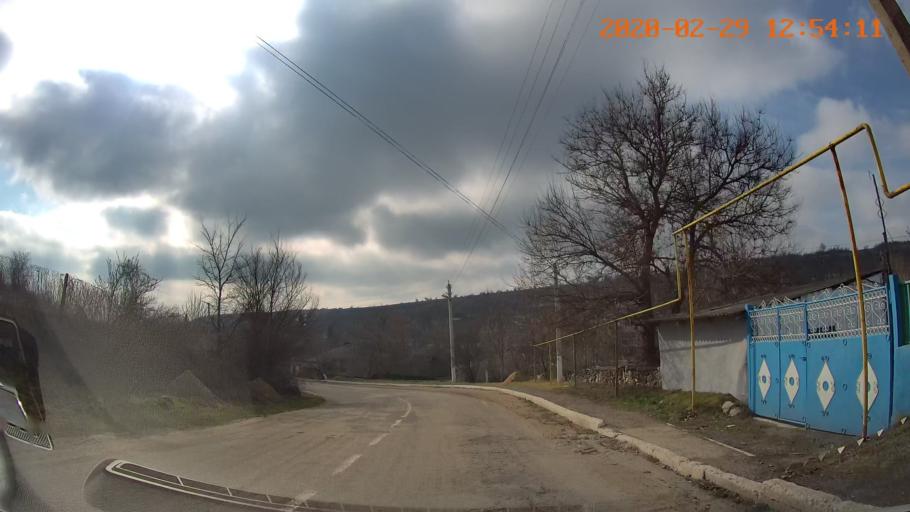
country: MD
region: Telenesti
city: Camenca
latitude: 48.1039
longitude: 28.7282
